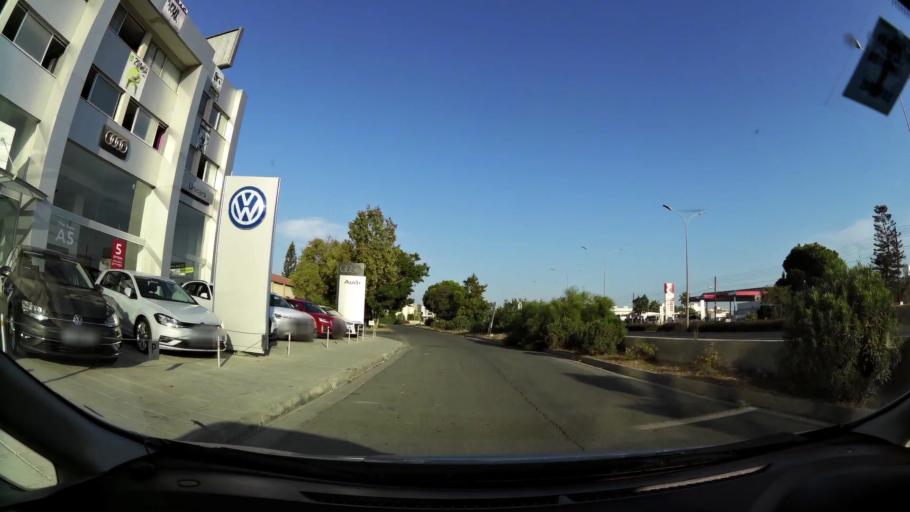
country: CY
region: Larnaka
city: Aradippou
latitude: 34.9345
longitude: 33.5930
